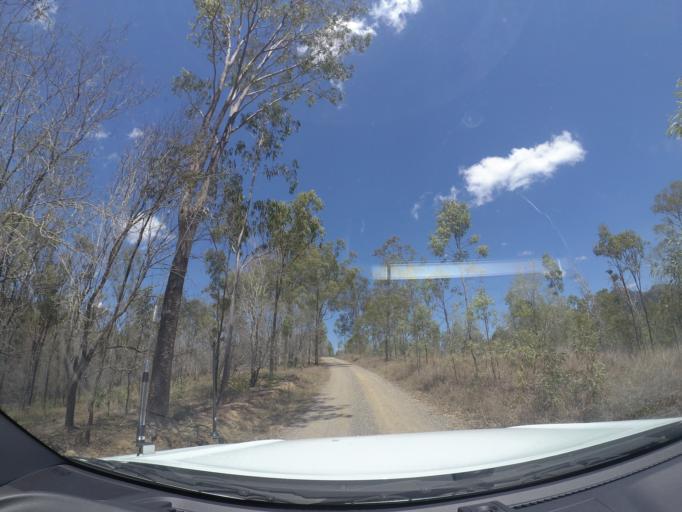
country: AU
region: Queensland
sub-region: Ipswich
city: Springfield Lakes
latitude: -27.8203
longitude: 152.8450
